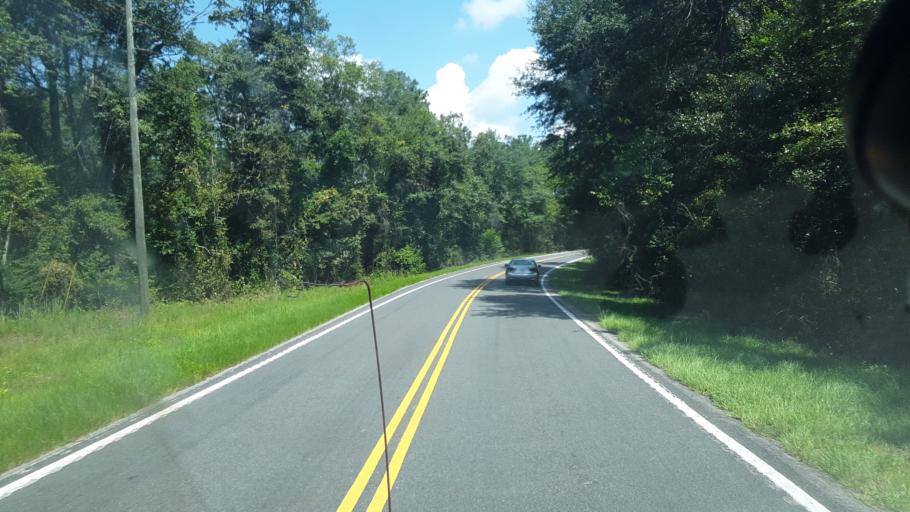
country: US
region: South Carolina
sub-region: Calhoun County
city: Oak Grove
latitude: 33.6432
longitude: -80.9956
